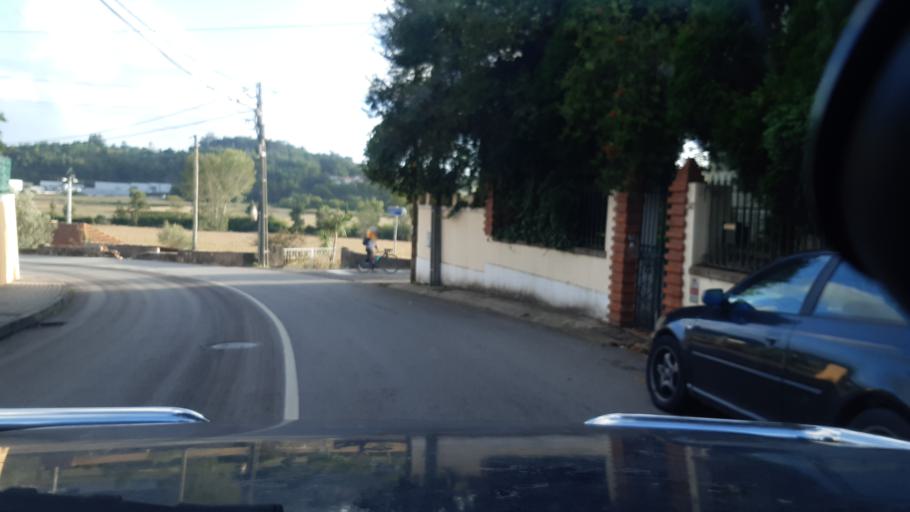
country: PT
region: Aveiro
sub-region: Agueda
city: Agueda
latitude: 40.5742
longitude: -8.4559
